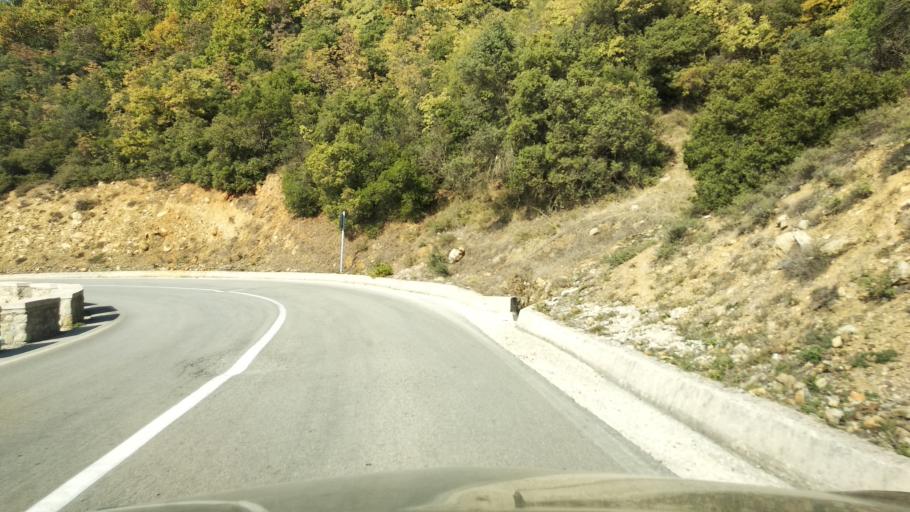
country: GR
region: Thessaly
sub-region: Trikala
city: Kastraki
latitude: 39.7208
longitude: 21.6362
